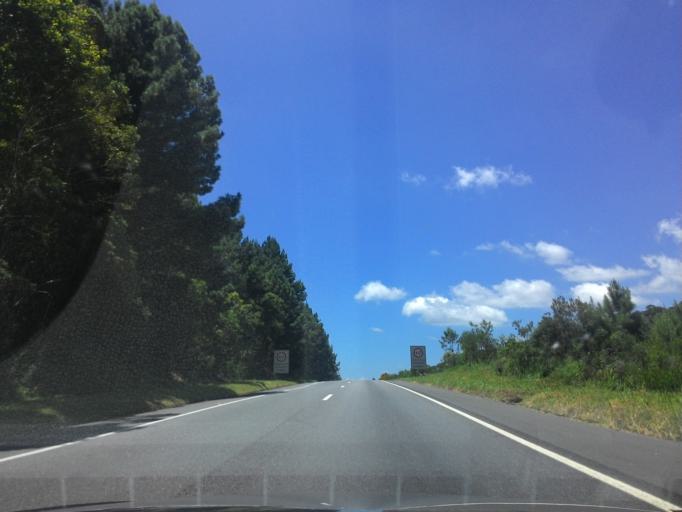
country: BR
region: Sao Paulo
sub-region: Cajati
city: Cajati
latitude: -24.9681
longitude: -48.4412
